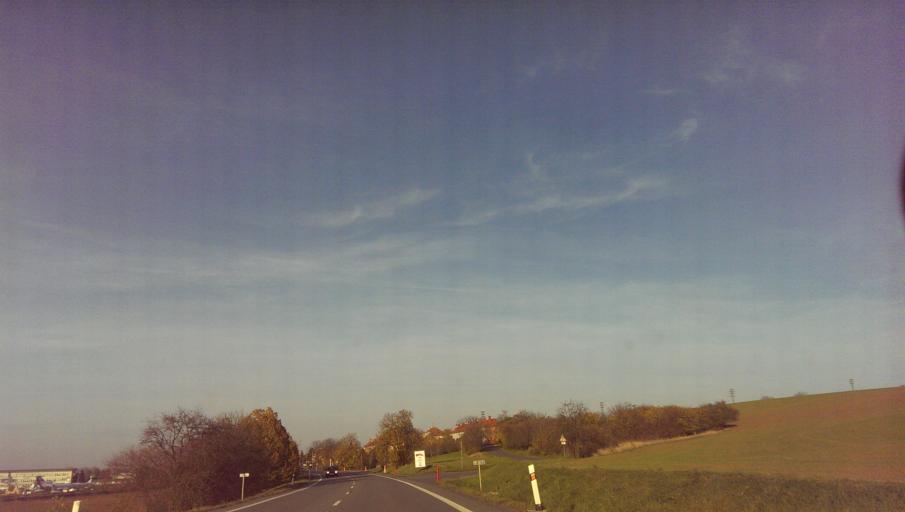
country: CZ
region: Zlin
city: Kunovice
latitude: 49.0291
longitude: 17.4582
